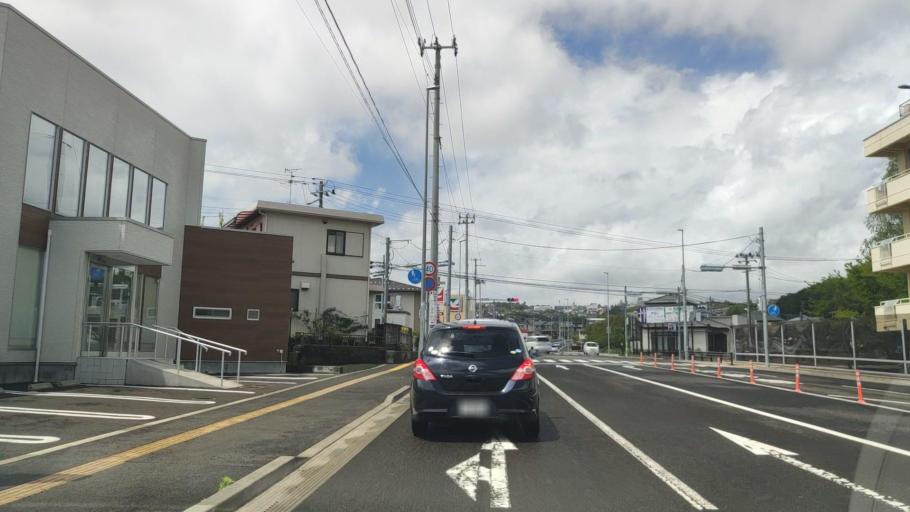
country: JP
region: Miyagi
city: Sendai
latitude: 38.2304
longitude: 140.8559
